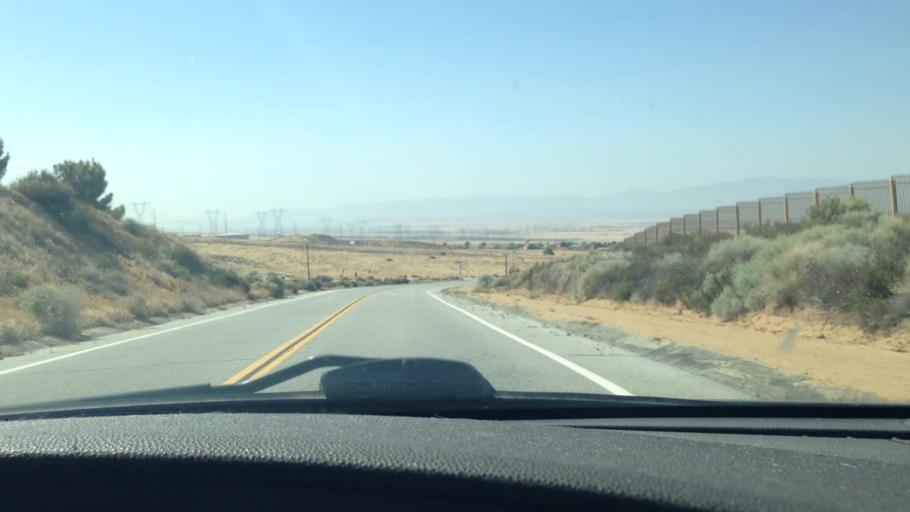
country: US
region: California
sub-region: Los Angeles County
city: Quartz Hill
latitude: 34.6333
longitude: -118.2516
